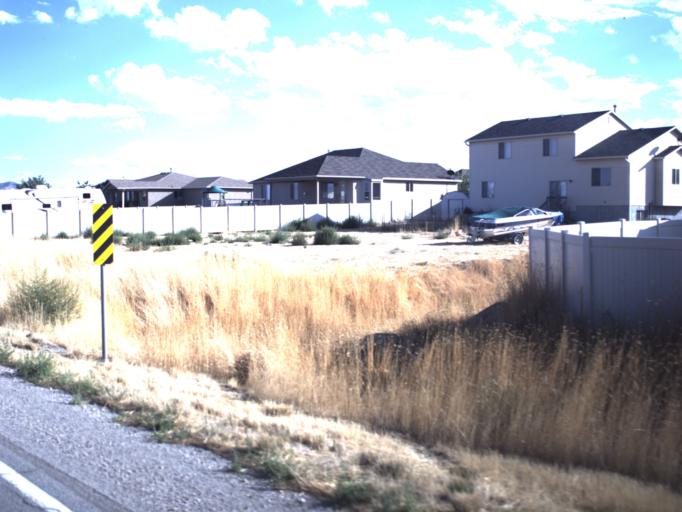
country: US
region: Utah
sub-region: Tooele County
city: Grantsville
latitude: 40.6052
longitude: -112.4876
